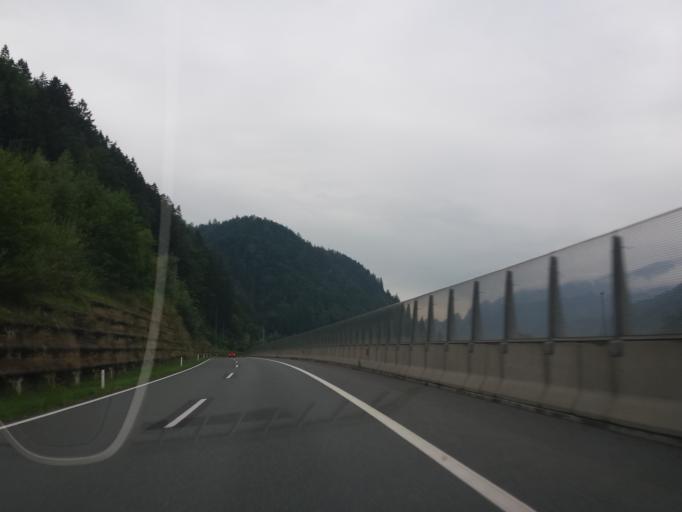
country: AT
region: Styria
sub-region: Politischer Bezirk Graz-Umgebung
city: Rothelstein
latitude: 47.3309
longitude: 15.3559
